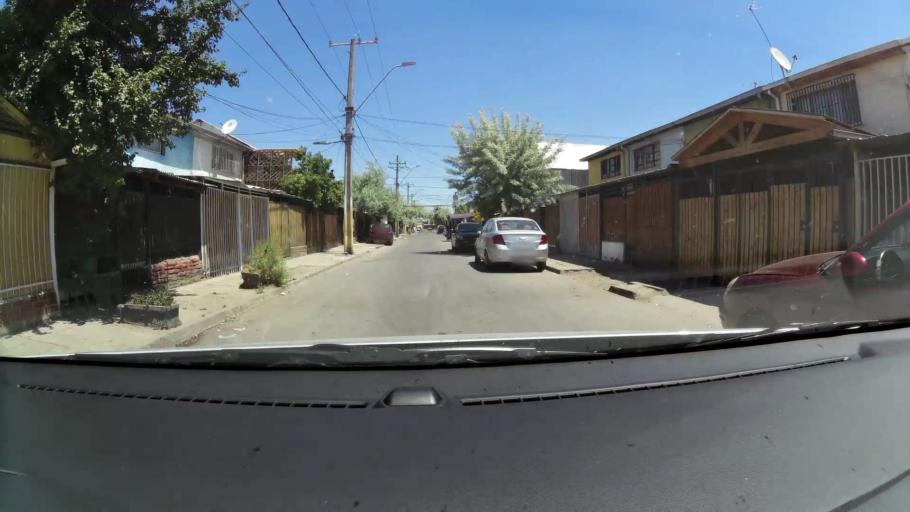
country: CL
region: Santiago Metropolitan
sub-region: Provincia de Maipo
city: San Bernardo
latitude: -33.5982
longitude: -70.6766
